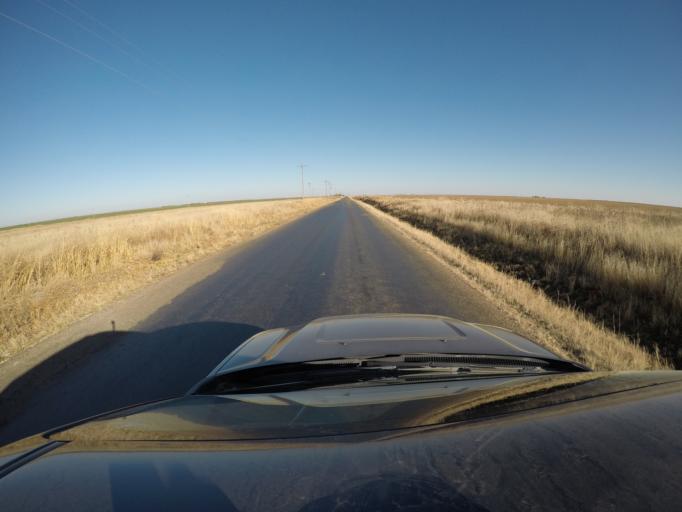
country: US
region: Texas
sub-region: Parmer County
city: Farwell
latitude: 34.3027
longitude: -103.0755
